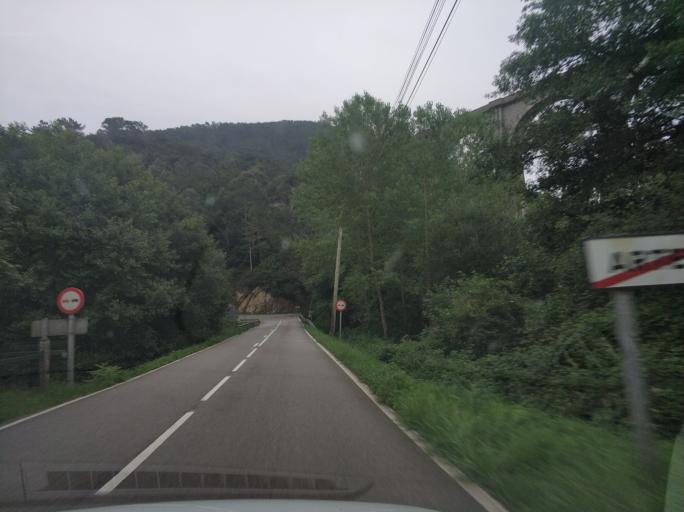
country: ES
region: Asturias
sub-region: Province of Asturias
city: Cudillero
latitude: 43.5529
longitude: -6.1929
